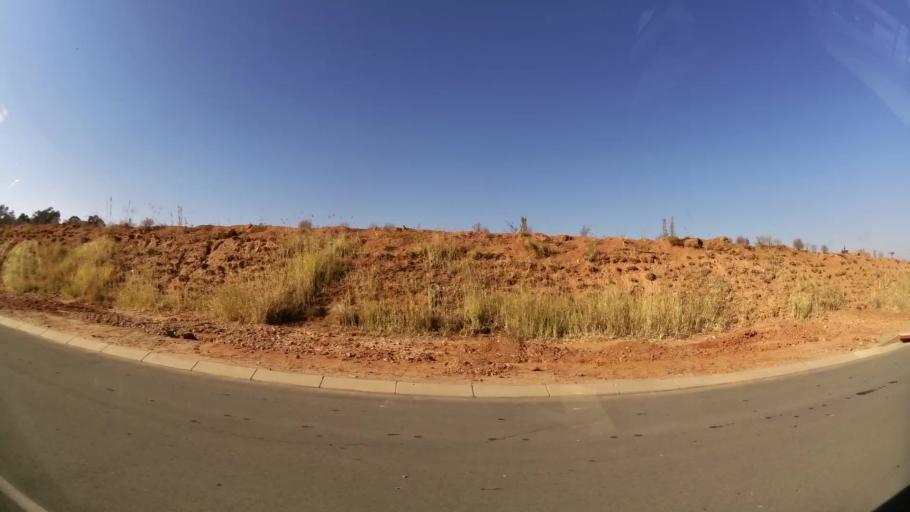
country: ZA
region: Gauteng
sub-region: City of Johannesburg Metropolitan Municipality
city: Modderfontein
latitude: -26.0492
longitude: 28.1704
